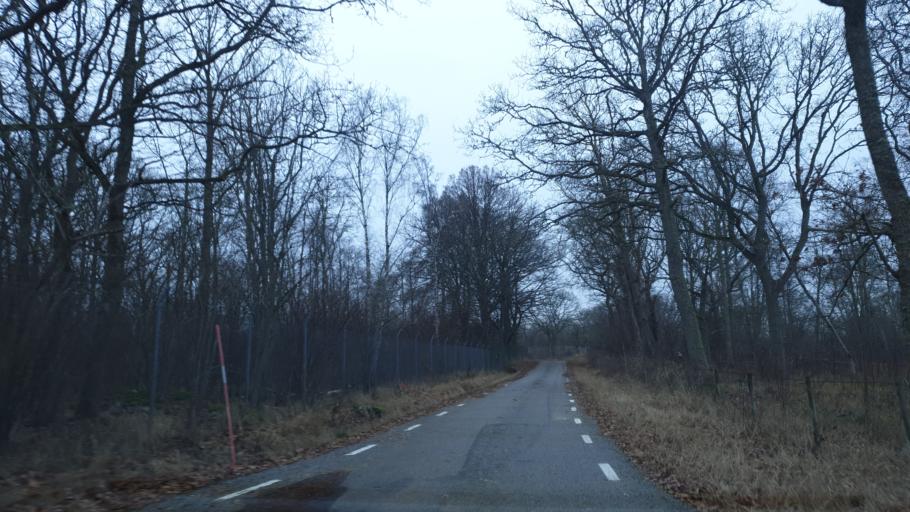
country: SE
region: Blekinge
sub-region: Karlskrona Kommun
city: Karlskrona
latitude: 56.1035
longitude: 15.6059
